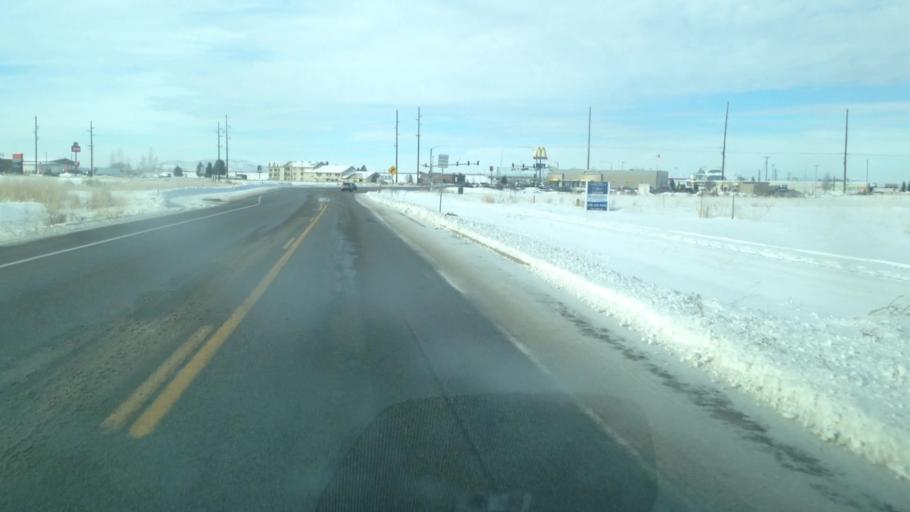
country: US
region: Idaho
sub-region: Madison County
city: Rexburg
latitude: 43.8035
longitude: -111.8050
